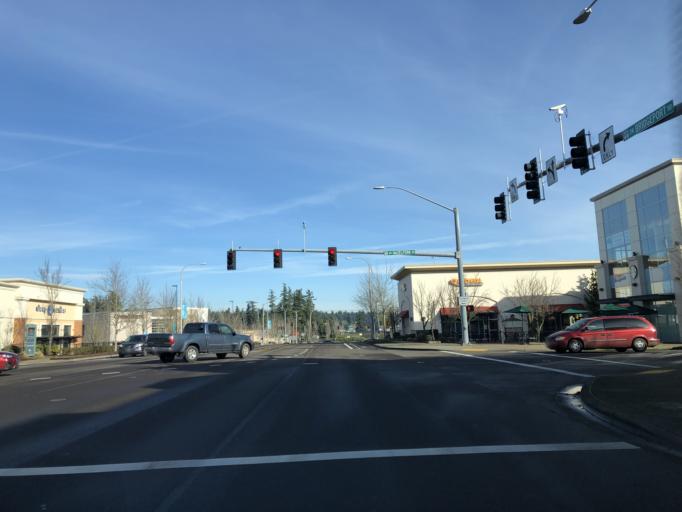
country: US
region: Oregon
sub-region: Washington County
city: Durham
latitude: 45.3949
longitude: -122.7517
